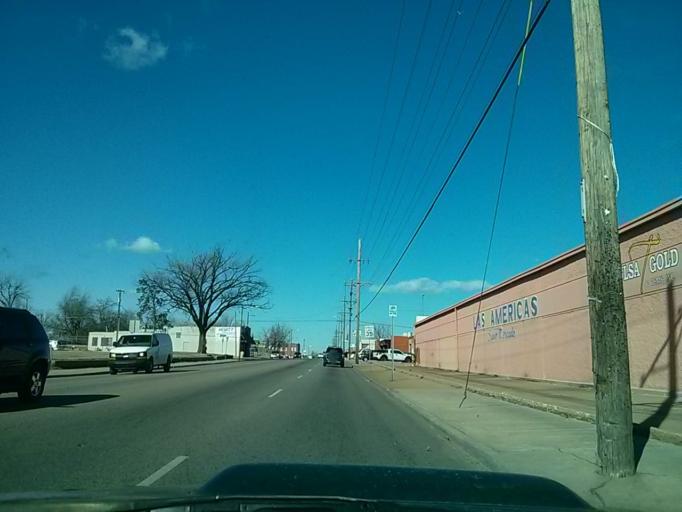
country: US
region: Oklahoma
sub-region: Tulsa County
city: Tulsa
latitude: 36.1617
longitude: -95.9581
